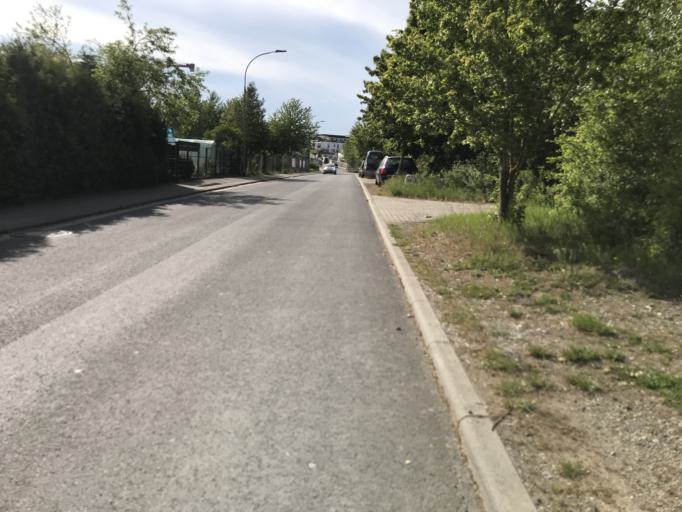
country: DE
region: Hesse
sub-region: Regierungsbezirk Giessen
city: Langgons
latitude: 50.4914
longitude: 8.6645
